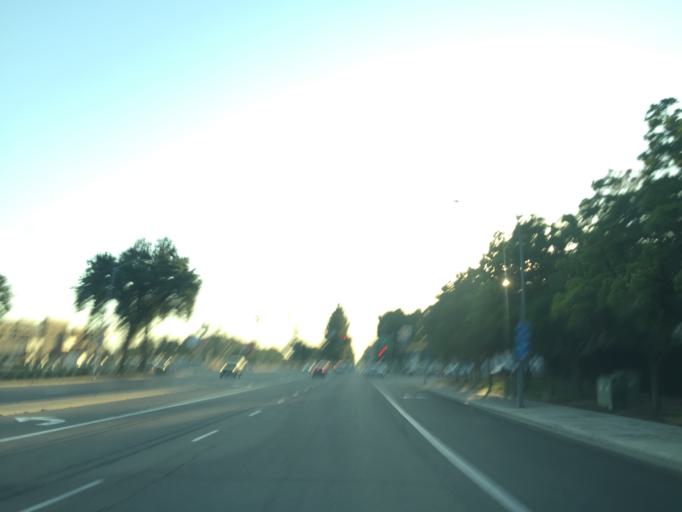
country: US
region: California
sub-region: Fresno County
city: Sunnyside
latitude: 36.7653
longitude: -119.7170
